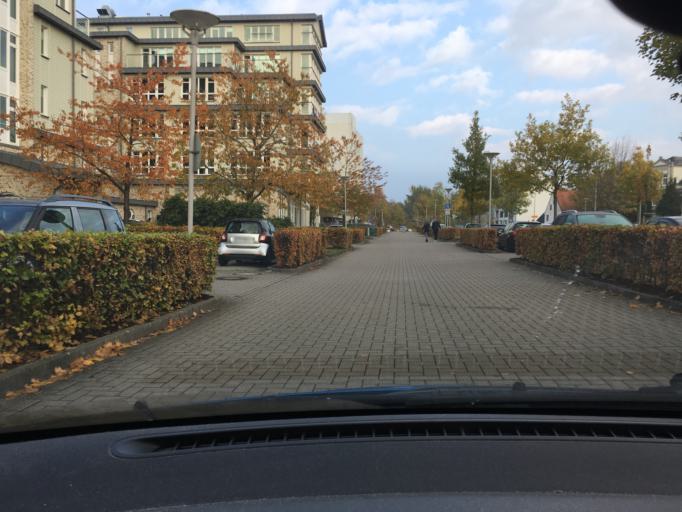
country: DE
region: Schleswig-Holstein
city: Flensburg
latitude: 54.7948
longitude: 9.4383
